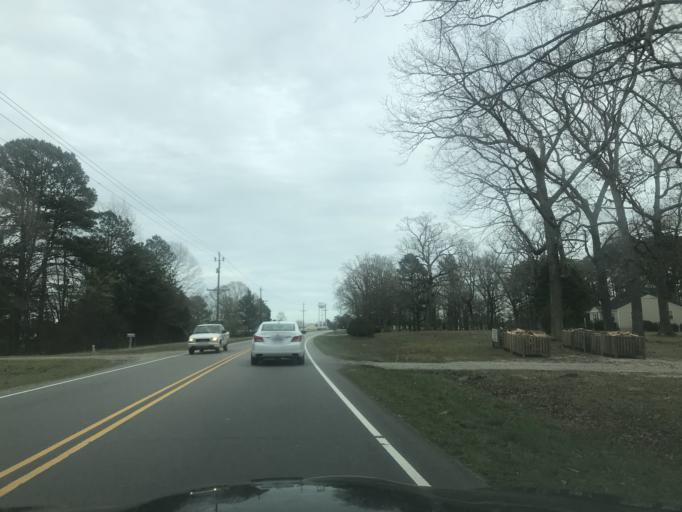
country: US
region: North Carolina
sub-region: Franklin County
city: Louisburg
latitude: 36.0872
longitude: -78.3251
